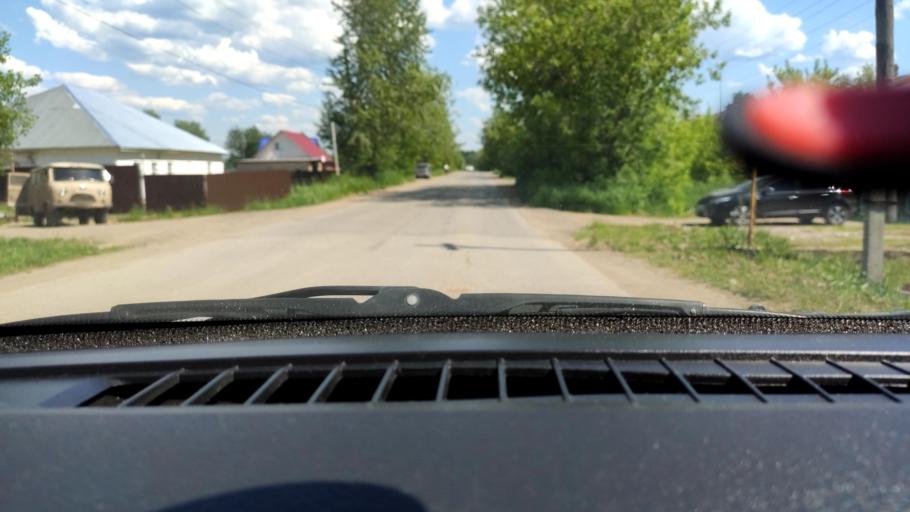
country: RU
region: Perm
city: Sylva
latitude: 58.0330
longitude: 56.7667
